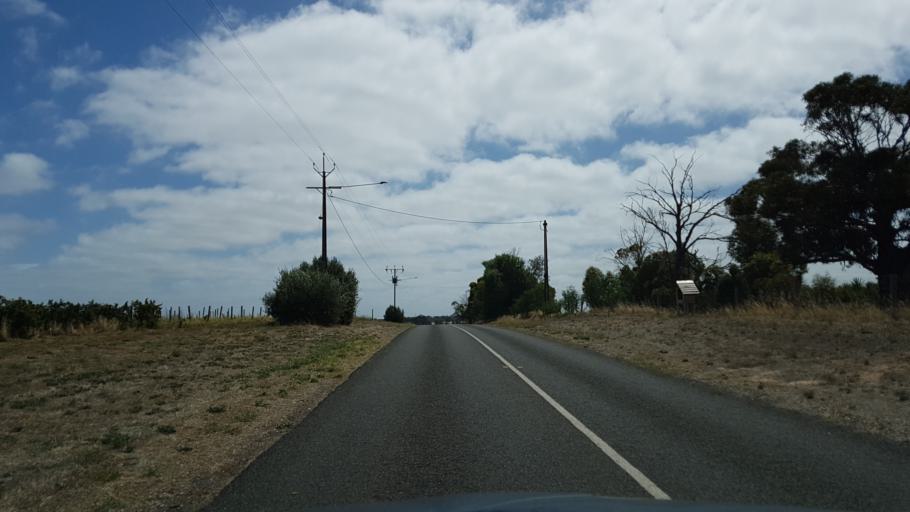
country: AU
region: South Australia
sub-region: Onkaparinga
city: McLaren Vale
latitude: -35.2152
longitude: 138.5177
